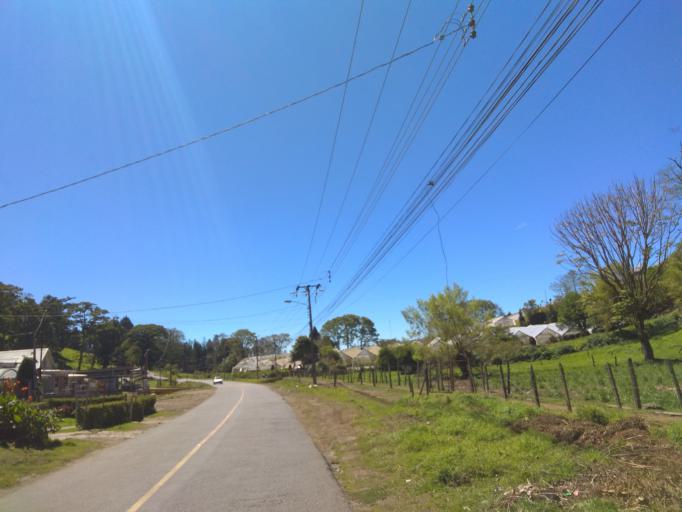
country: CR
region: Cartago
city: Tres Rios
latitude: 9.9464
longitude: -83.9314
